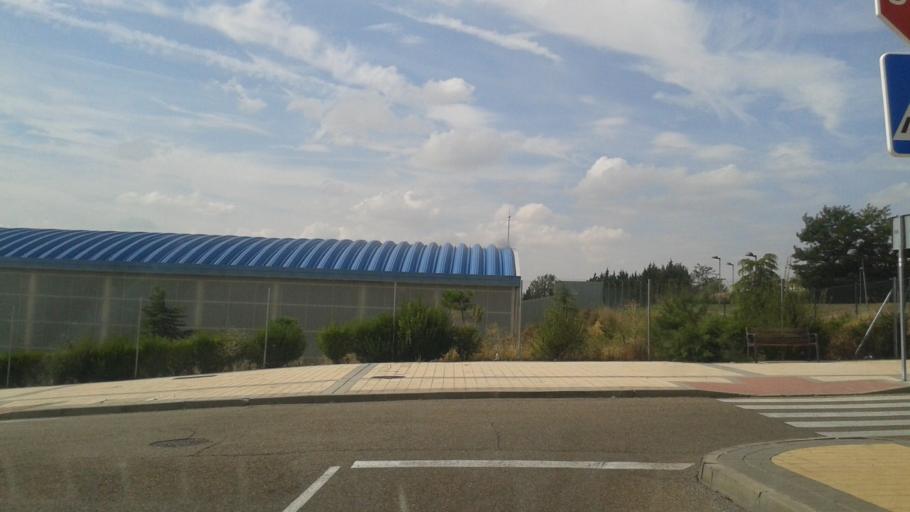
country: ES
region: Castille and Leon
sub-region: Provincia de Valladolid
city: Arroyo
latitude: 41.6244
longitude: -4.7757
